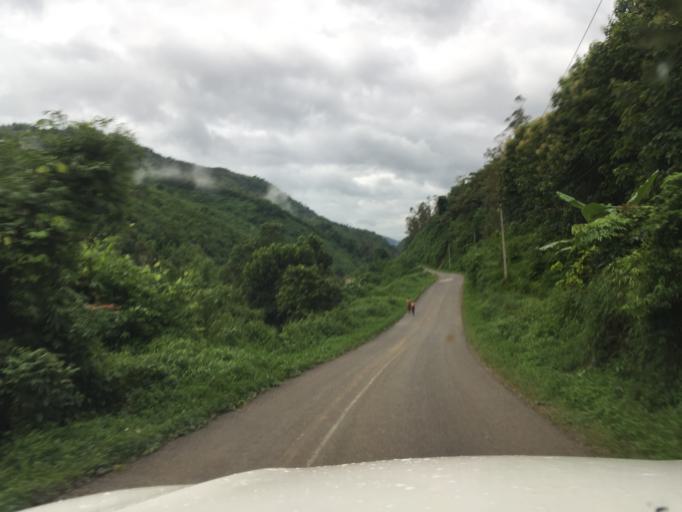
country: LA
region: Oudomxai
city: Muang La
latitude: 20.9981
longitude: 102.2318
